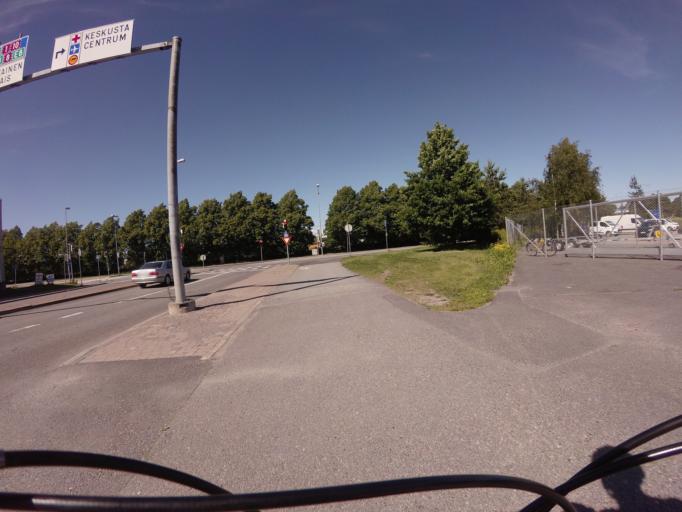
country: FI
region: Varsinais-Suomi
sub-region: Turku
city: Turku
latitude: 60.4438
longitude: 22.2324
